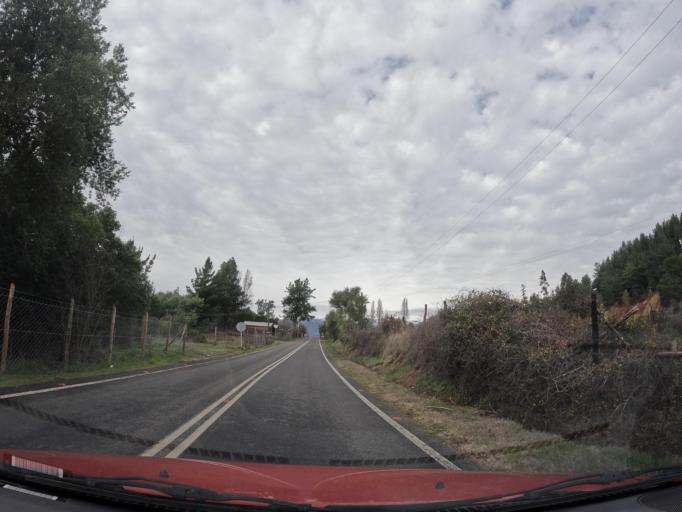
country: CL
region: Maule
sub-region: Provincia de Linares
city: Linares
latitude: -35.9277
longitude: -71.4320
